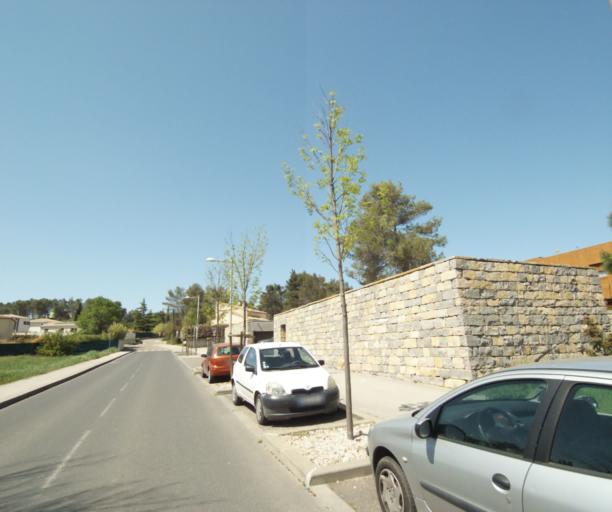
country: FR
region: Languedoc-Roussillon
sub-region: Departement de l'Herault
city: Prades-le-Lez
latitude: 43.6941
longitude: 3.8720
